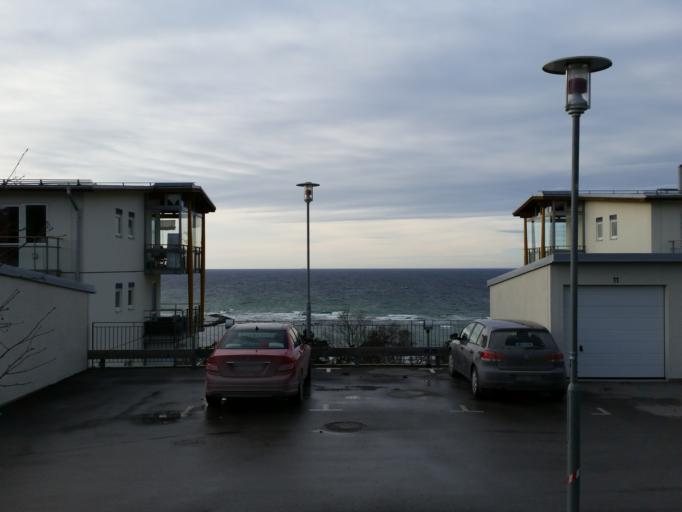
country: SE
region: Gotland
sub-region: Gotland
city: Visby
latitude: 57.6698
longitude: 18.3353
